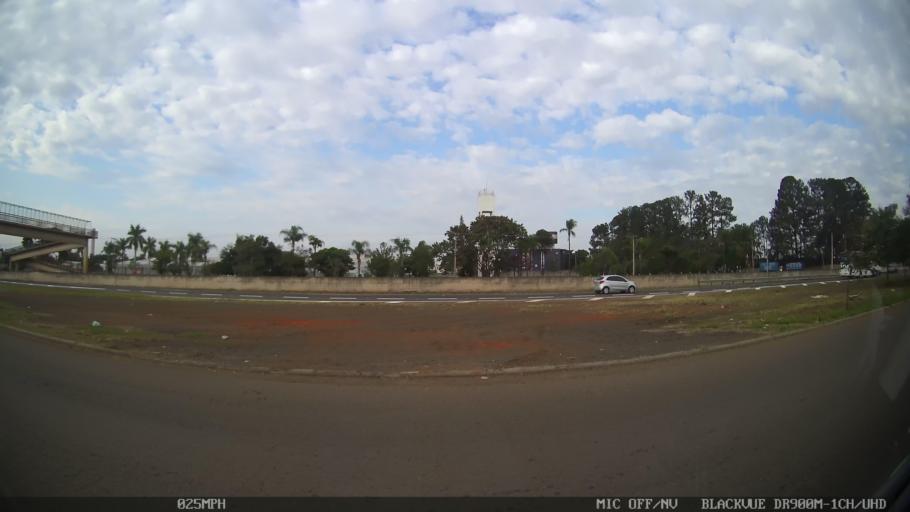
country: BR
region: Sao Paulo
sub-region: Santa Barbara D'Oeste
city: Santa Barbara d'Oeste
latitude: -22.7636
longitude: -47.3814
